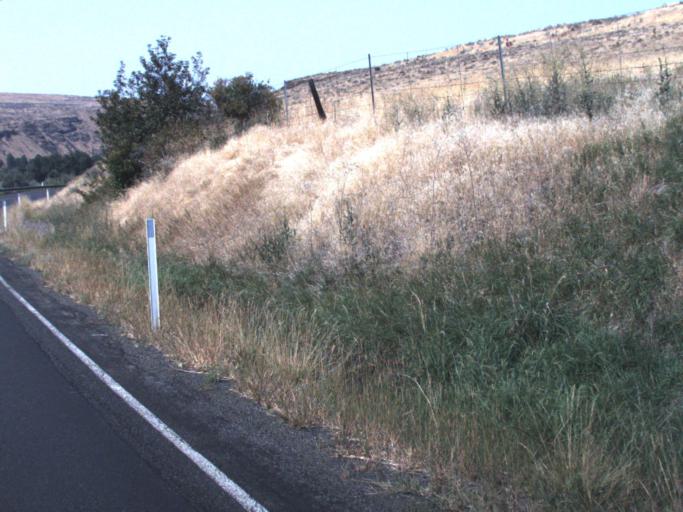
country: US
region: Washington
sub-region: Kittitas County
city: Kittitas
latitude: 46.8223
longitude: -120.4586
